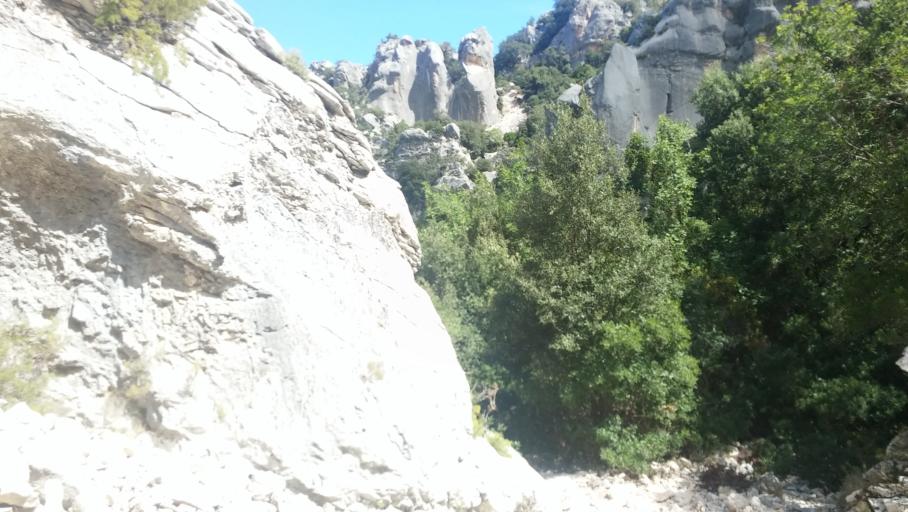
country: IT
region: Sardinia
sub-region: Provincia di Ogliastra
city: Baunei
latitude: 40.1046
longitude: 9.6886
